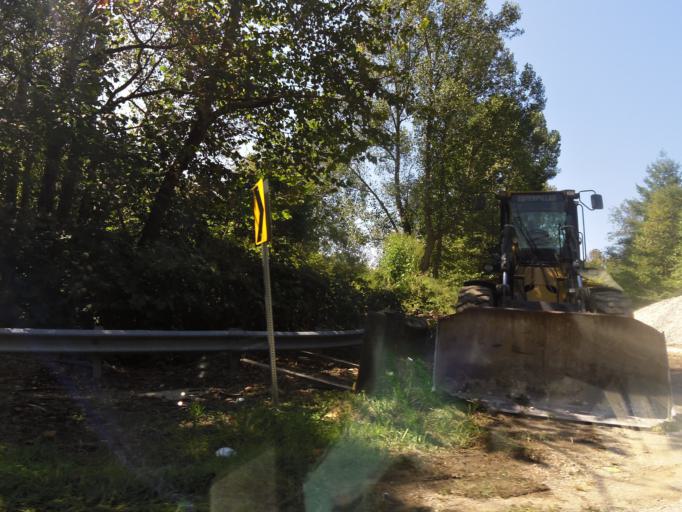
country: US
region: Kentucky
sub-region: Clay County
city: Manchester
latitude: 37.0856
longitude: -83.6904
